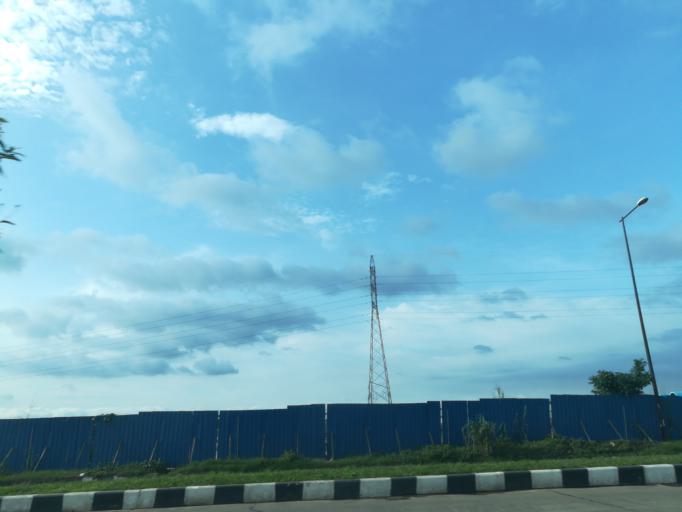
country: NG
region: Lagos
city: Ebute Ikorodu
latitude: 6.6185
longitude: 3.4611
